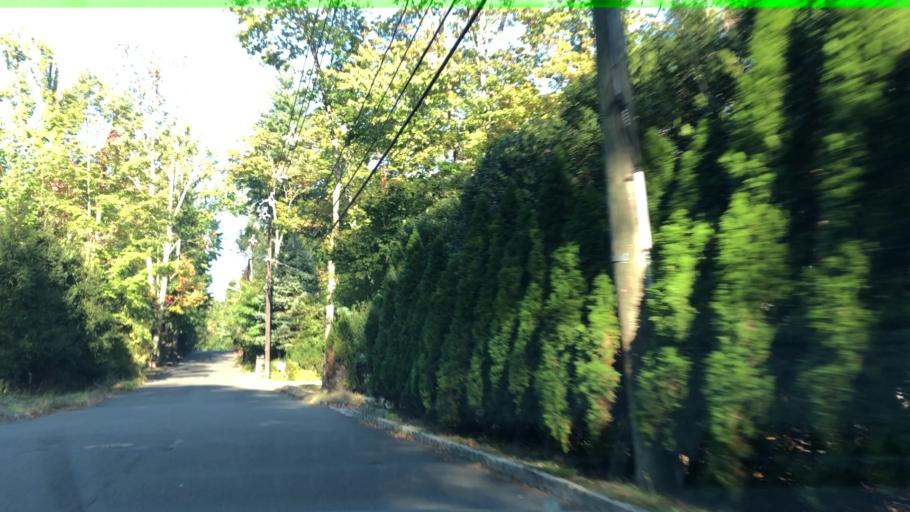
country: US
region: New Jersey
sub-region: Bergen County
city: Woodcliff Lake
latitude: 41.0322
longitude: -74.0603
